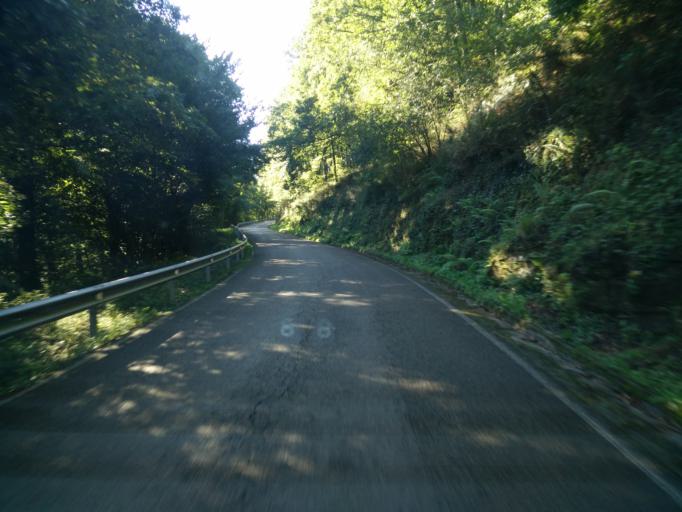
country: ES
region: Cantabria
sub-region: Provincia de Cantabria
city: San Pedro del Romeral
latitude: 43.1222
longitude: -3.8105
